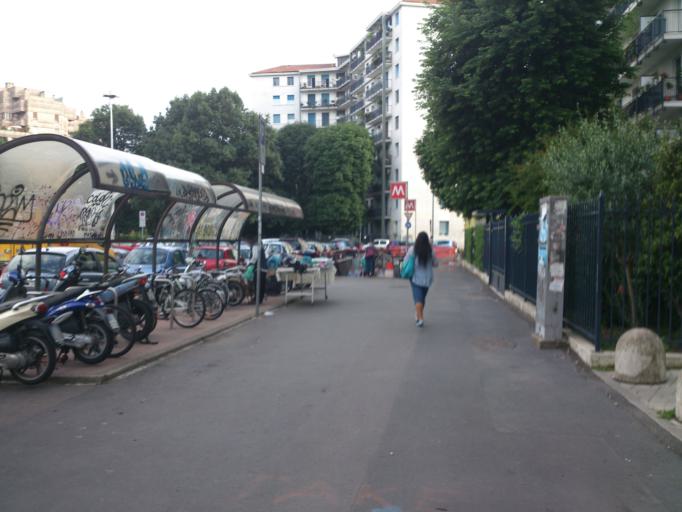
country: IT
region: Lombardy
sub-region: Citta metropolitana di Milano
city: Romano Banco
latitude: 45.4619
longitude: 9.1359
